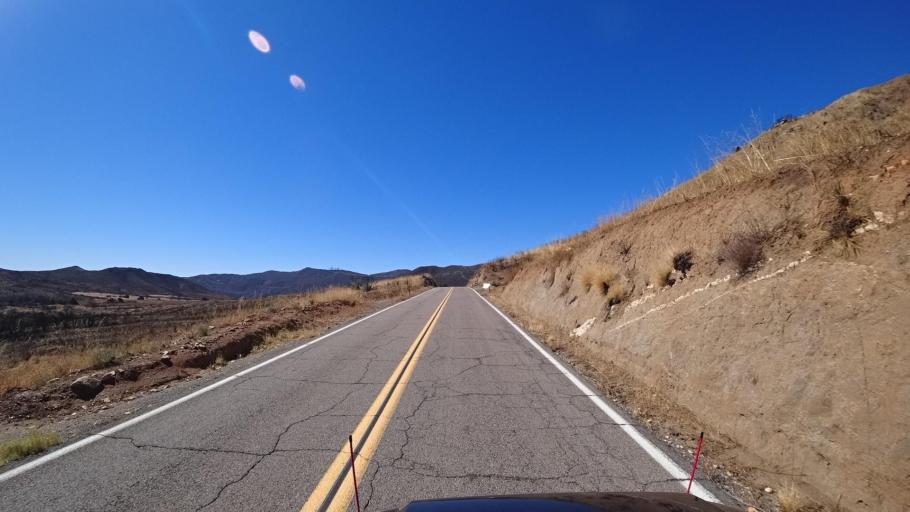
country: US
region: California
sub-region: San Diego County
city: Alpine
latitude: 32.7275
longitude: -116.6962
